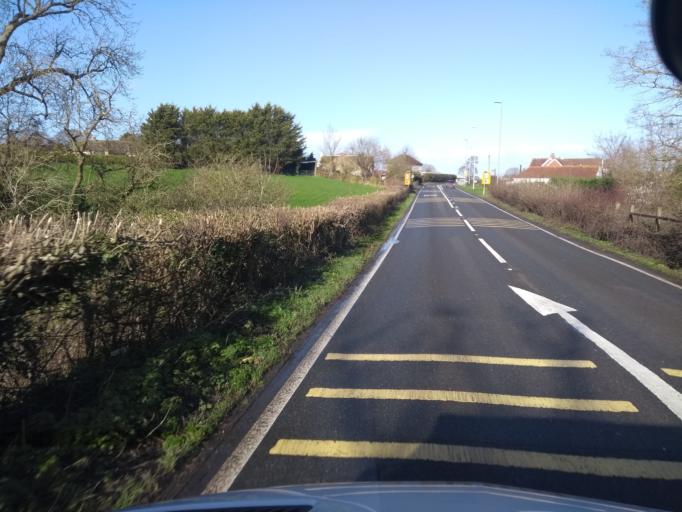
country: GB
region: England
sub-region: Somerset
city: Ilchester
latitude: 50.9716
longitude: -2.6690
